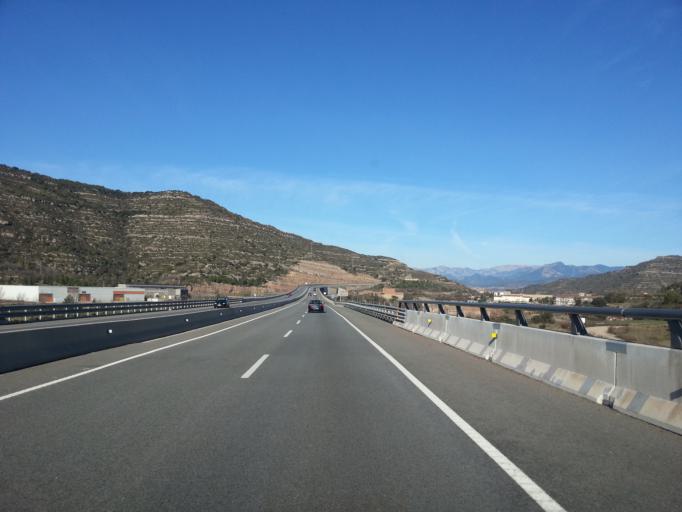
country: ES
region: Catalonia
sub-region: Provincia de Barcelona
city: Puig-reig
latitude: 41.9799
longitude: 1.8867
